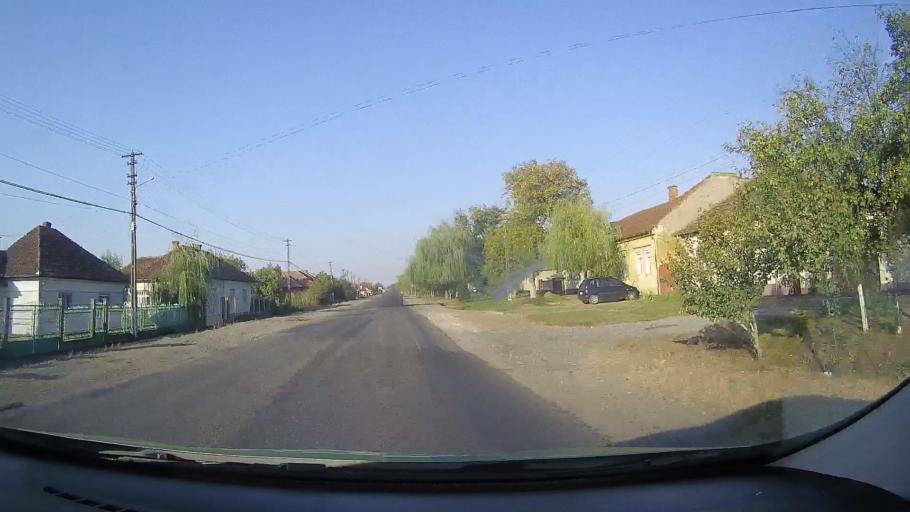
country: RO
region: Arad
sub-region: Comuna Siria
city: Galsa
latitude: 46.2772
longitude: 21.6430
